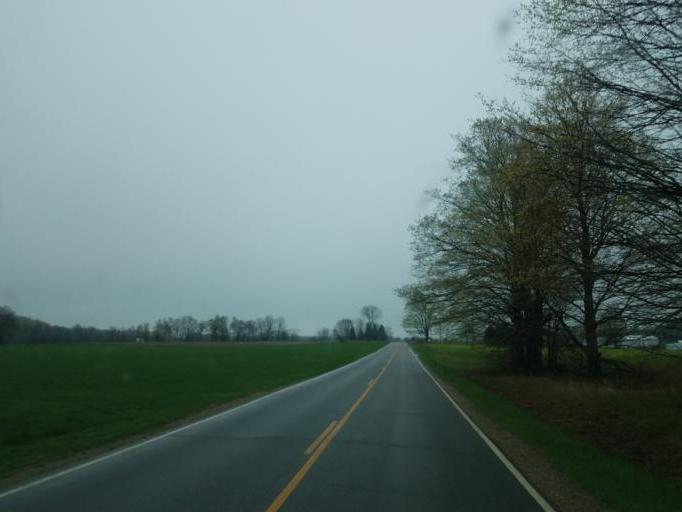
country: US
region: Michigan
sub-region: Isabella County
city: Lake Isabella
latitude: 43.5250
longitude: -84.9438
